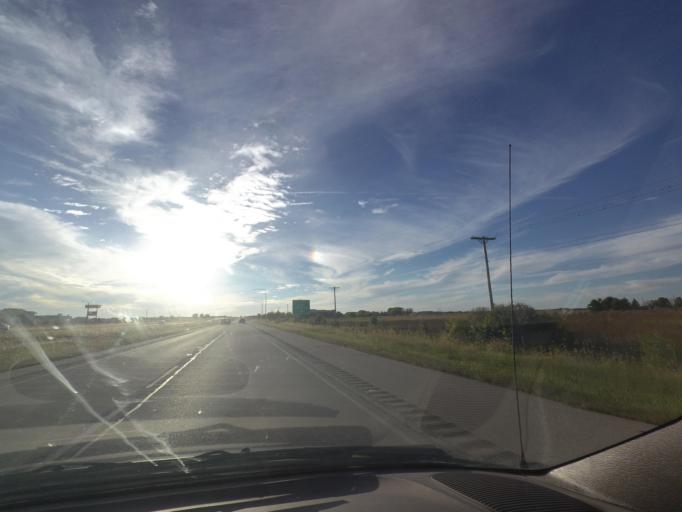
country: US
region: Illinois
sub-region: Sangamon County
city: Jerome
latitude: 39.7522
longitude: -89.7407
